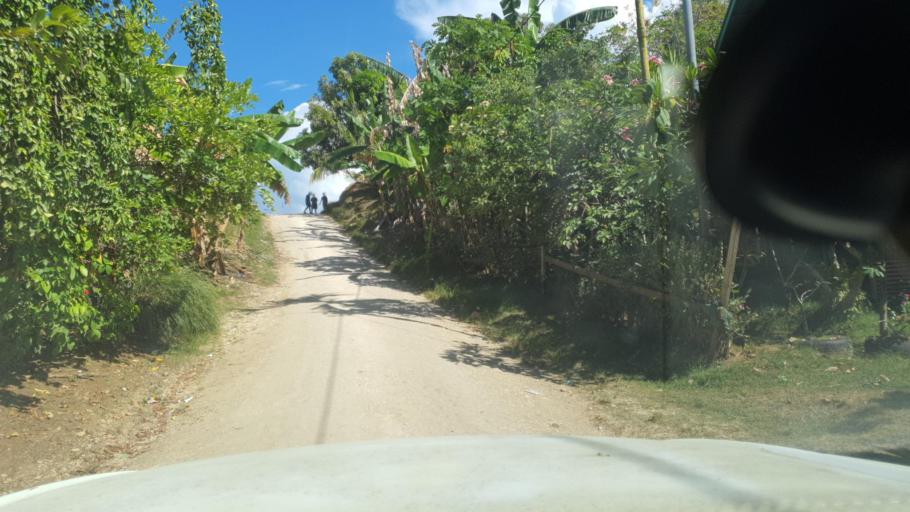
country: SB
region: Guadalcanal
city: Honiara
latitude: -9.4474
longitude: 159.9756
